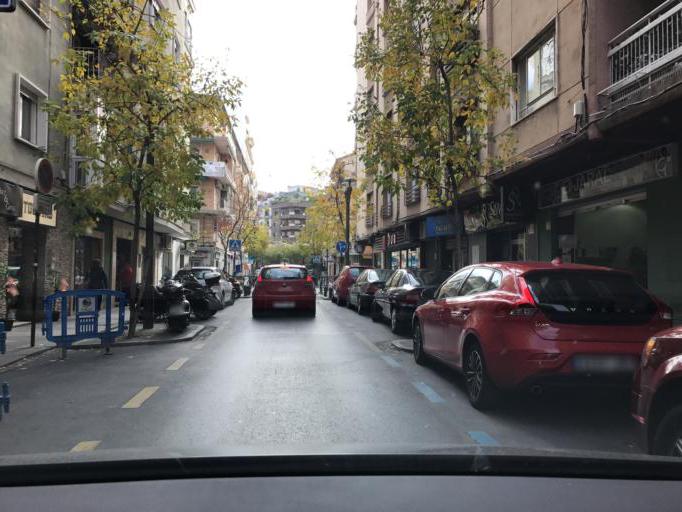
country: ES
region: Andalusia
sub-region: Provincia de Granada
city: Granada
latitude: 37.1697
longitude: -3.6039
